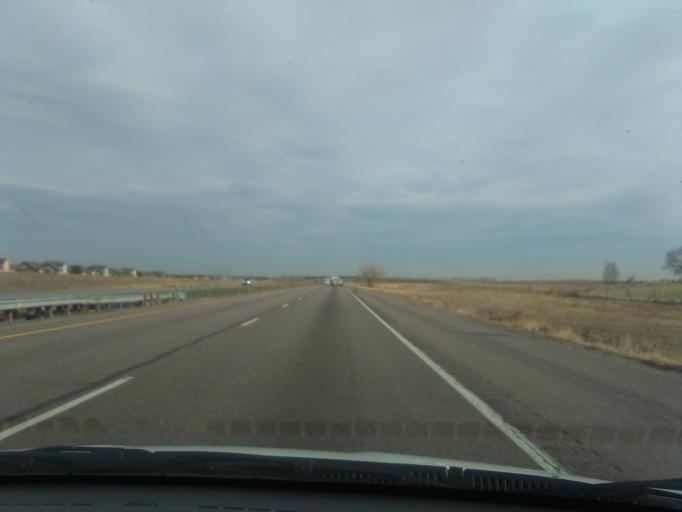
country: US
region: Colorado
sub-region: Adams County
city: Derby
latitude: 39.8922
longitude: -104.8555
